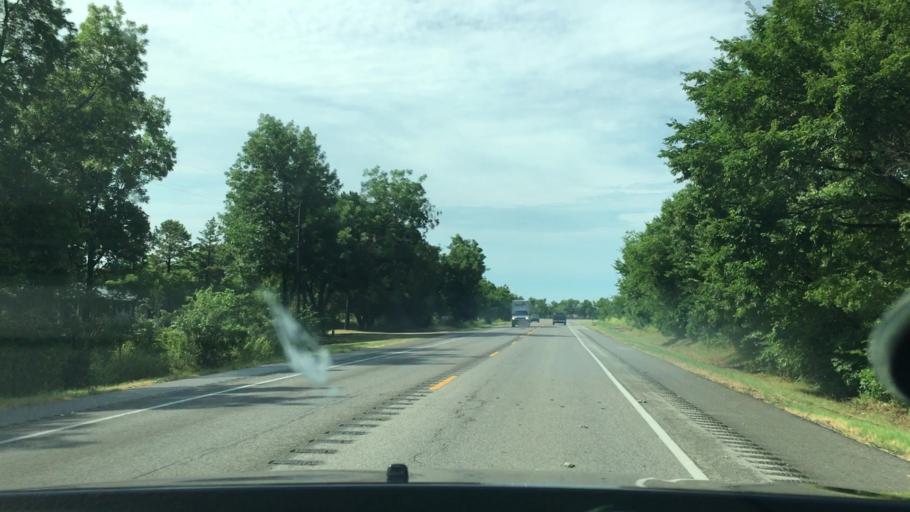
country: US
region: Oklahoma
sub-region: Murray County
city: Sulphur
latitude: 34.5348
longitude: -96.9674
